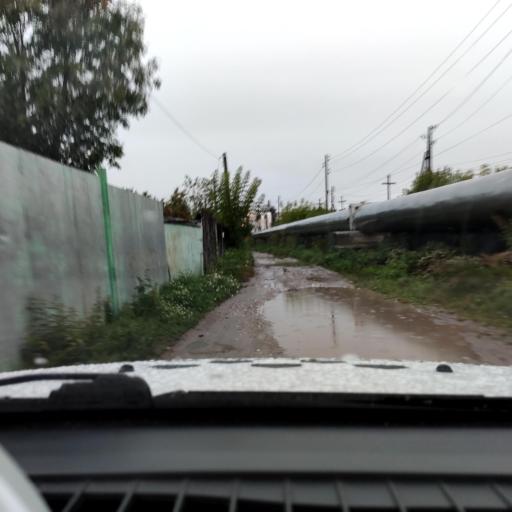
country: RU
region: Perm
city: Kondratovo
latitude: 57.9562
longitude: 56.1409
